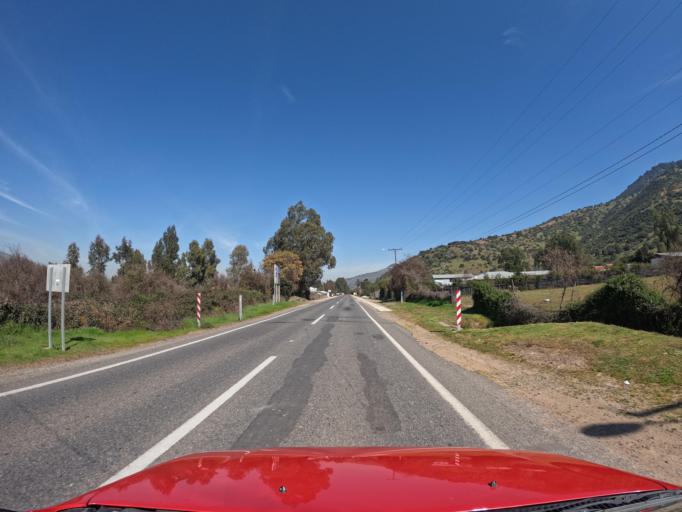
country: CL
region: Maule
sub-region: Provincia de Curico
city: Rauco
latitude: -35.0498
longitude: -71.5998
